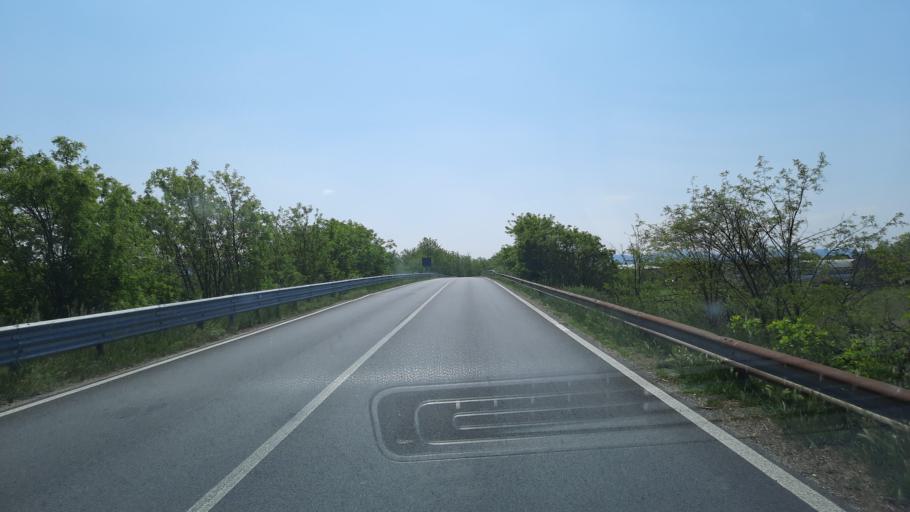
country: IT
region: Piedmont
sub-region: Provincia di Vercelli
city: Crescentino
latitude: 45.1955
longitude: 8.0976
